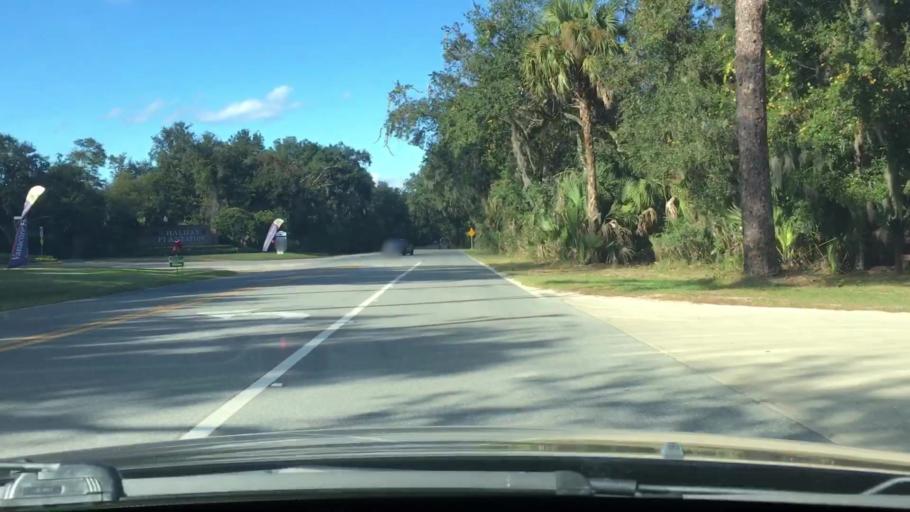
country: US
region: Florida
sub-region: Volusia County
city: Ormond-by-the-Sea
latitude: 29.3877
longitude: -81.1323
